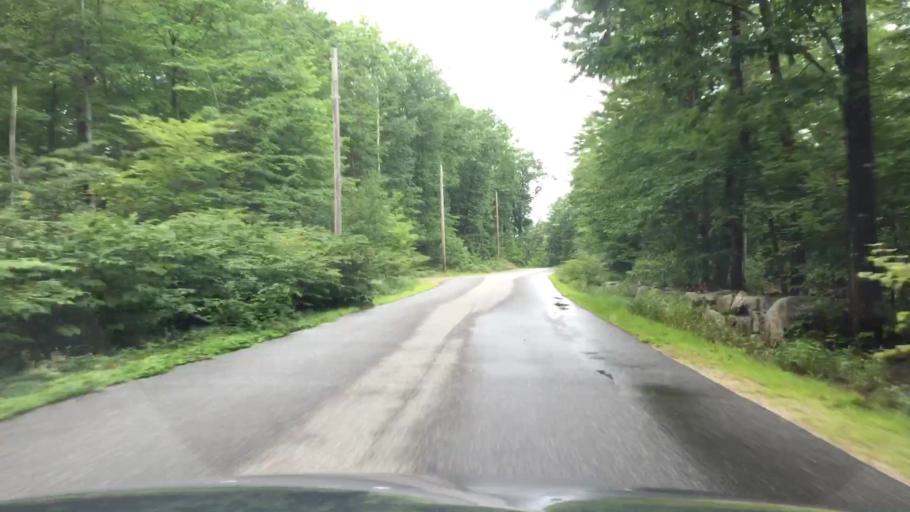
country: US
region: New Hampshire
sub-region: Carroll County
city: Center Harbor
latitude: 43.7187
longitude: -71.4830
